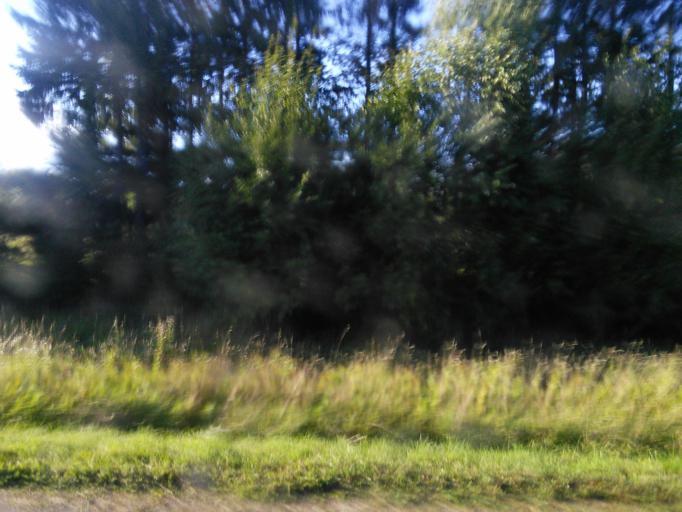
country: RU
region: Jaroslavl
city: Poshekhon'ye
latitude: 58.4823
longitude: 39.0656
